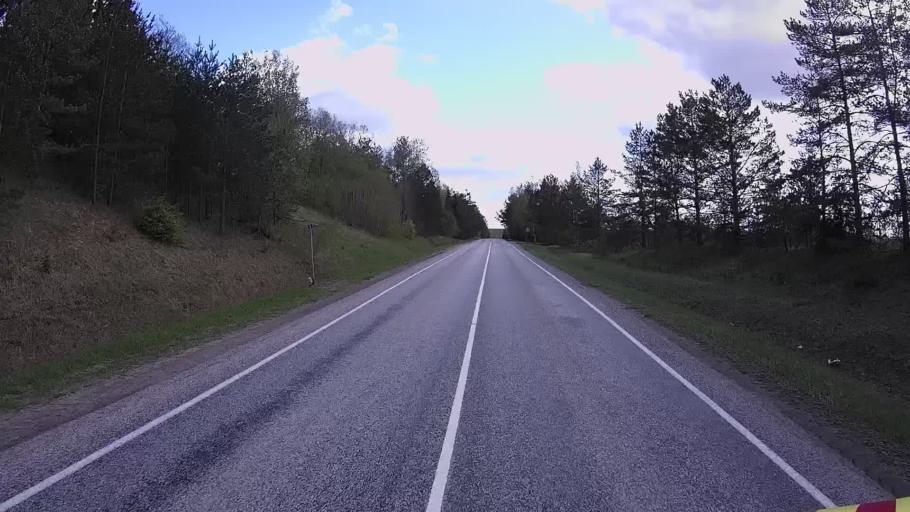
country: EE
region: Jogevamaa
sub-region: Jogeva linn
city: Jogeva
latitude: 58.7833
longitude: 26.4754
